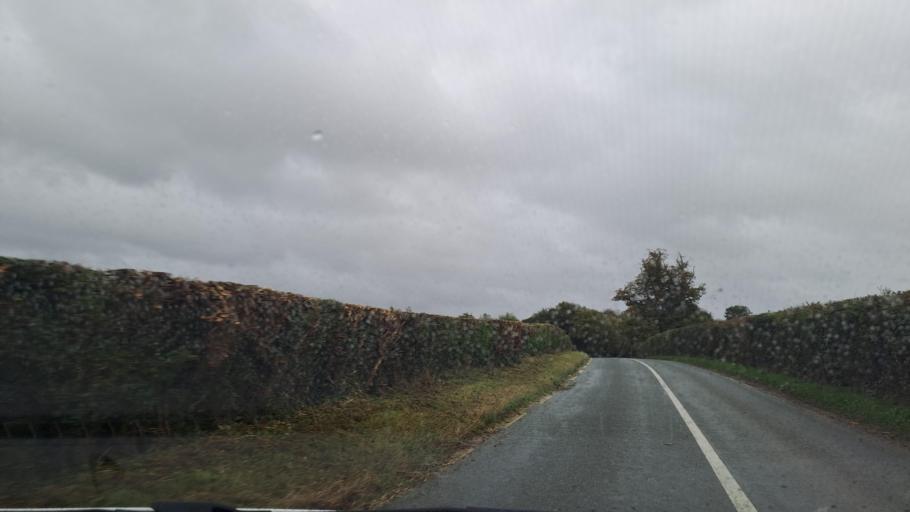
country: IE
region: Leinster
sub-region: Lu
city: Dundalk
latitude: 53.9632
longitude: -6.4630
